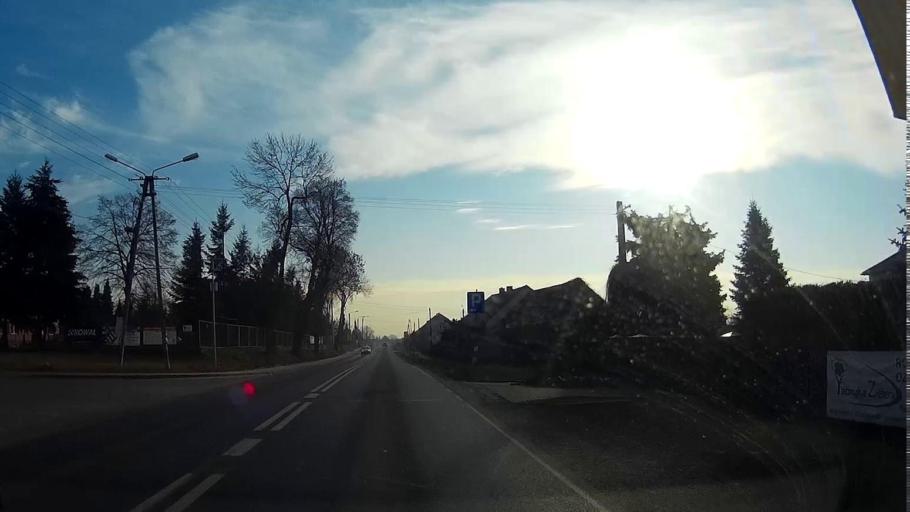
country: PL
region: Lesser Poland Voivodeship
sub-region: Powiat chrzanowski
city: Babice
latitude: 50.0725
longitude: 19.4429
